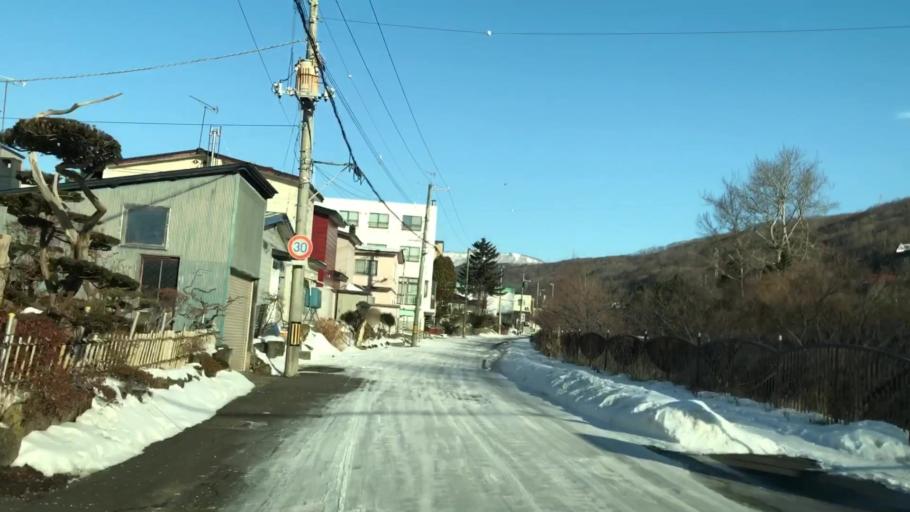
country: JP
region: Hokkaido
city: Muroran
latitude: 42.3747
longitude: 141.0375
